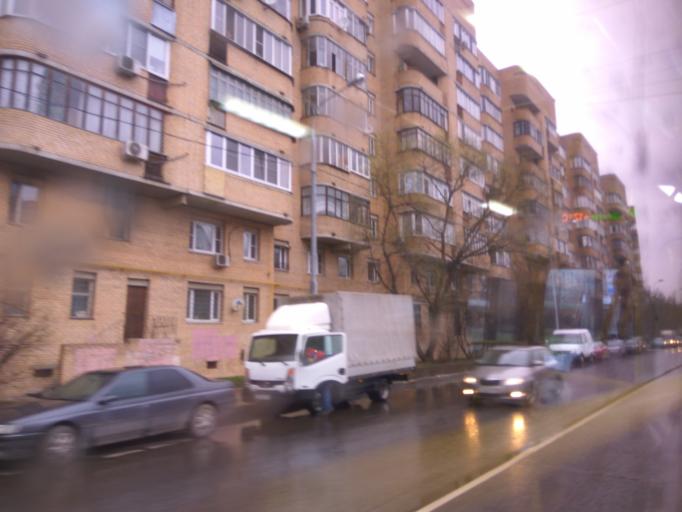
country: RU
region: Moscow
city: Vagonoremont
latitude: 55.8926
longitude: 37.5327
